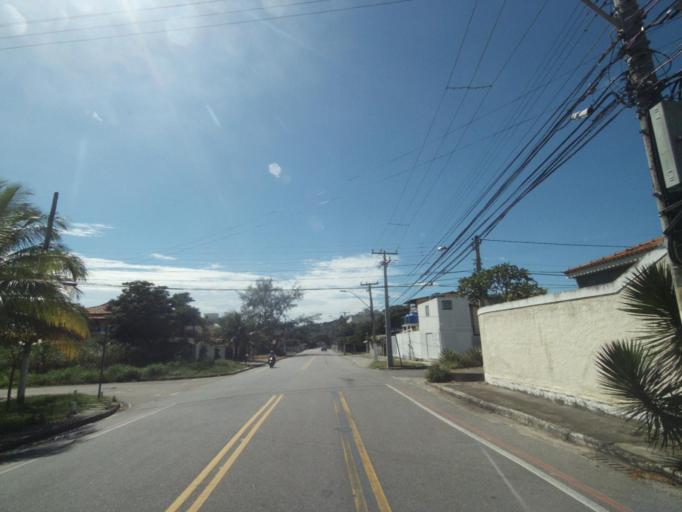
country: BR
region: Rio de Janeiro
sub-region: Niteroi
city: Niteroi
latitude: -22.9539
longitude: -43.0736
